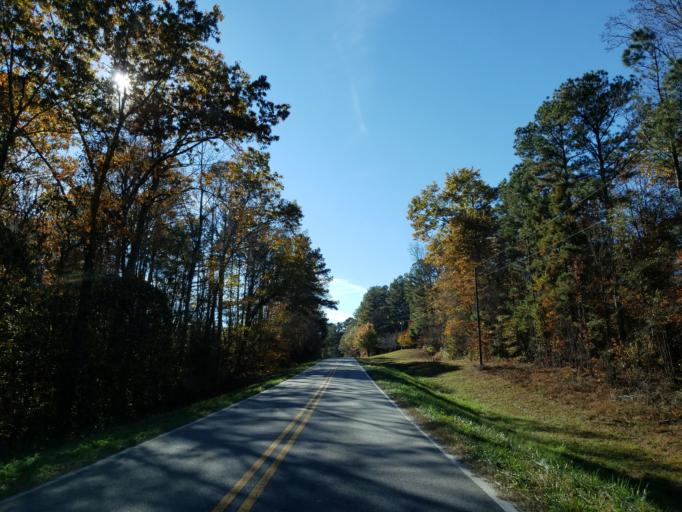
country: US
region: Alabama
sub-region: Cleburne County
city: Heflin
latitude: 33.5918
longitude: -85.6332
